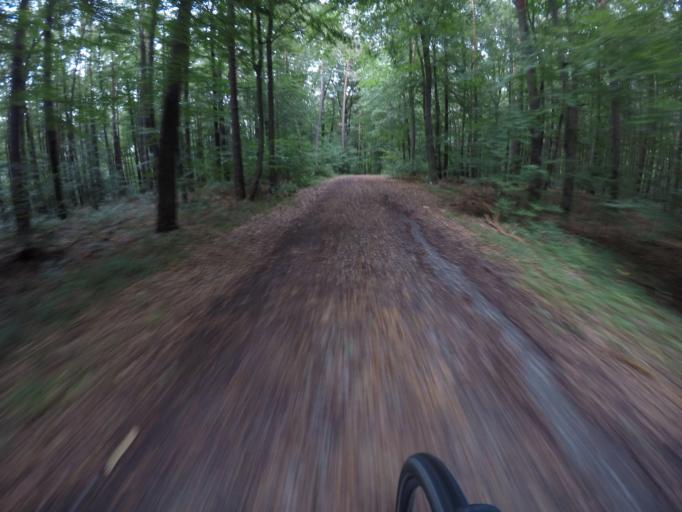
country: DE
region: Baden-Wuerttemberg
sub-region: Regierungsbezirk Stuttgart
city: Steinenbronn
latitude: 48.7251
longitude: 9.0829
